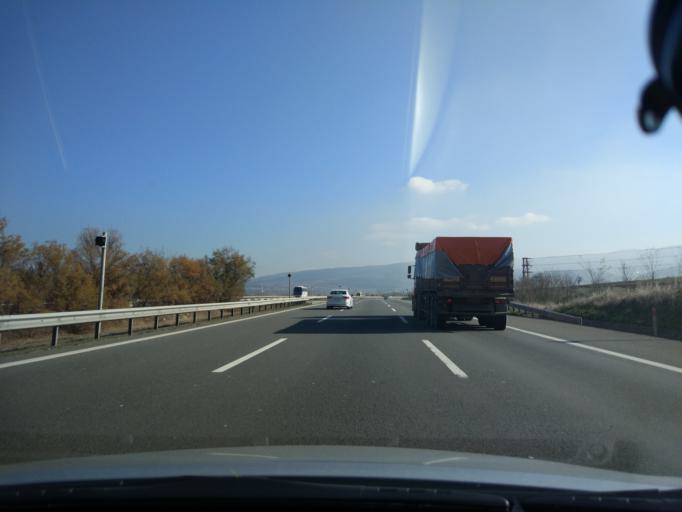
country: TR
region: Bolu
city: Bolu
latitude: 40.7677
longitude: 31.7463
